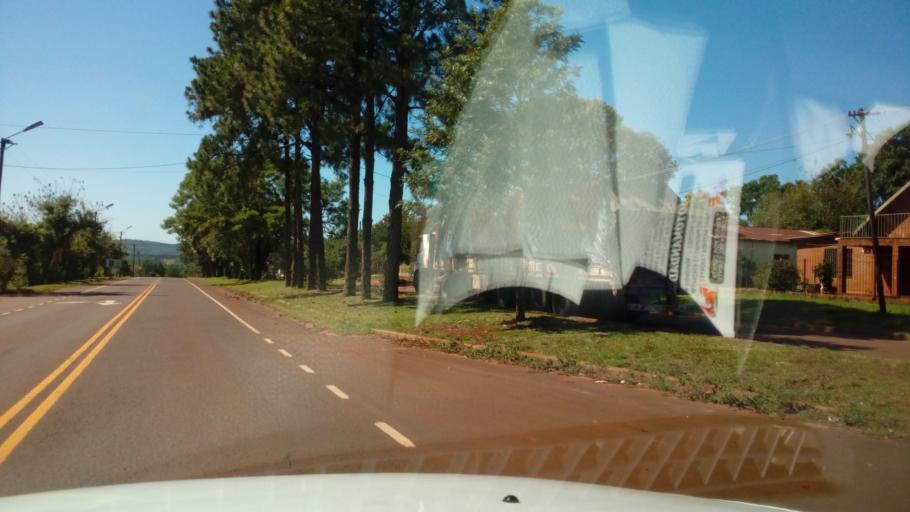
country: AR
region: Misiones
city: Bonpland
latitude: -27.4807
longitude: -55.4739
